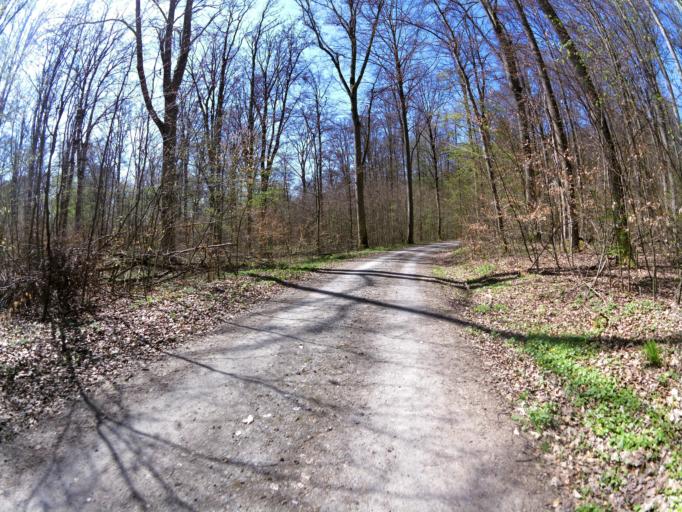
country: DE
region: Bavaria
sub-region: Regierungsbezirk Unterfranken
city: Hettstadt
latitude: 49.8199
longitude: 9.8111
